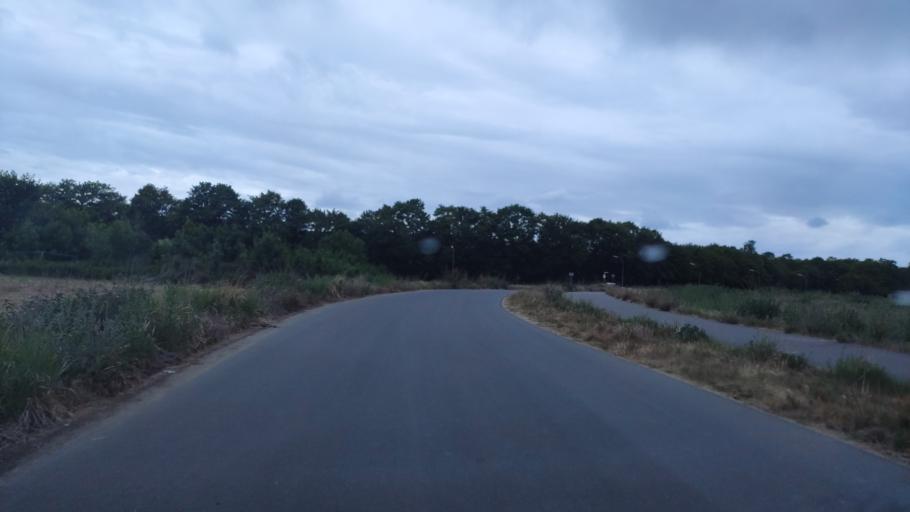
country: DE
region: North Rhine-Westphalia
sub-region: Regierungsbezirk Dusseldorf
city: Neuss
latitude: 51.1707
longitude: 6.6641
